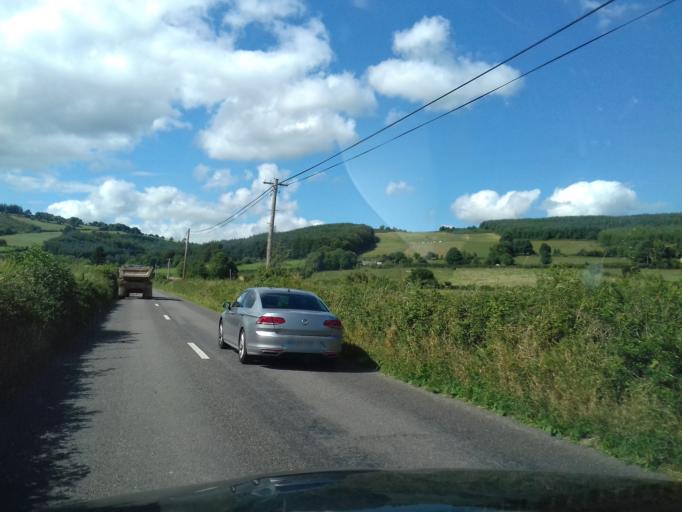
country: IE
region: Munster
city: Carrick-on-Suir
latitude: 52.3970
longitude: -7.4741
